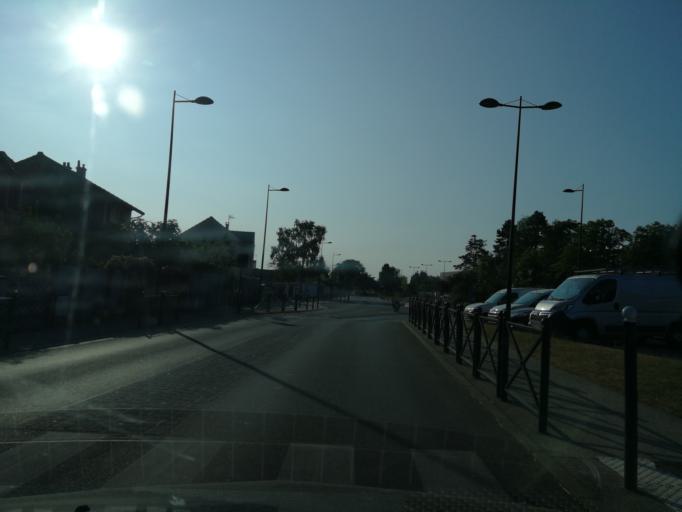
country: FR
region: Ile-de-France
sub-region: Departement de l'Essonne
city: Limours
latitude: 48.6434
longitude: 2.0819
